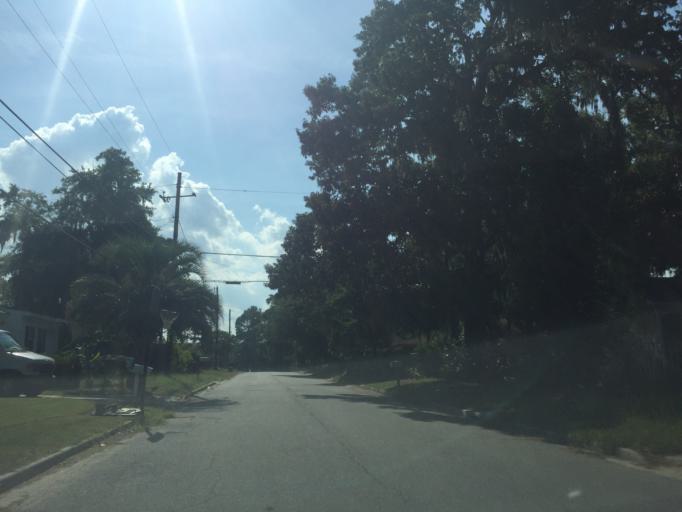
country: US
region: Georgia
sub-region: Chatham County
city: Isle of Hope
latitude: 31.9855
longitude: -81.1032
